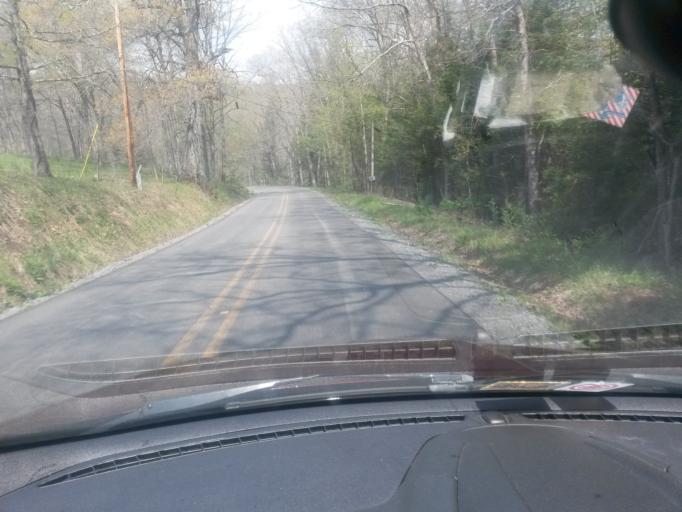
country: US
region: West Virginia
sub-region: Pocahontas County
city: Marlinton
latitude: 38.1090
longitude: -80.2243
